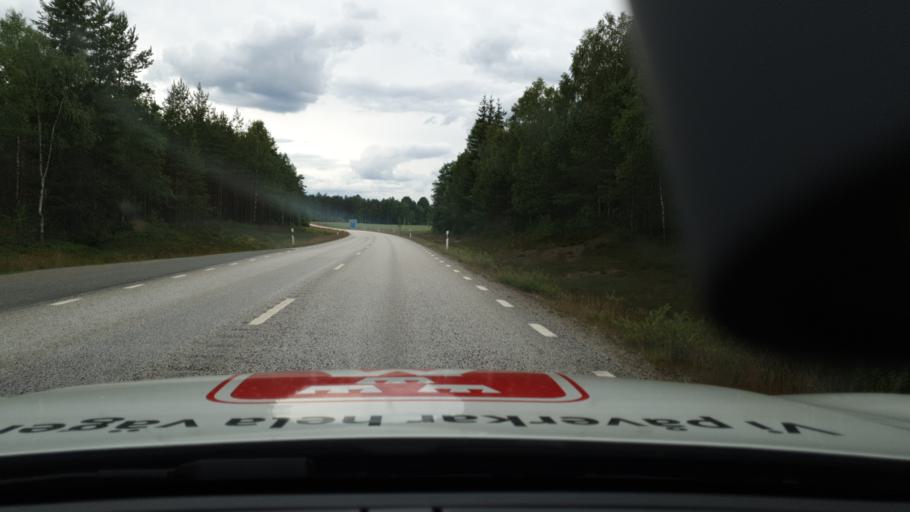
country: SE
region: Joenkoeping
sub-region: Gnosjo Kommun
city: Hillerstorp
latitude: 57.2885
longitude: 13.8322
